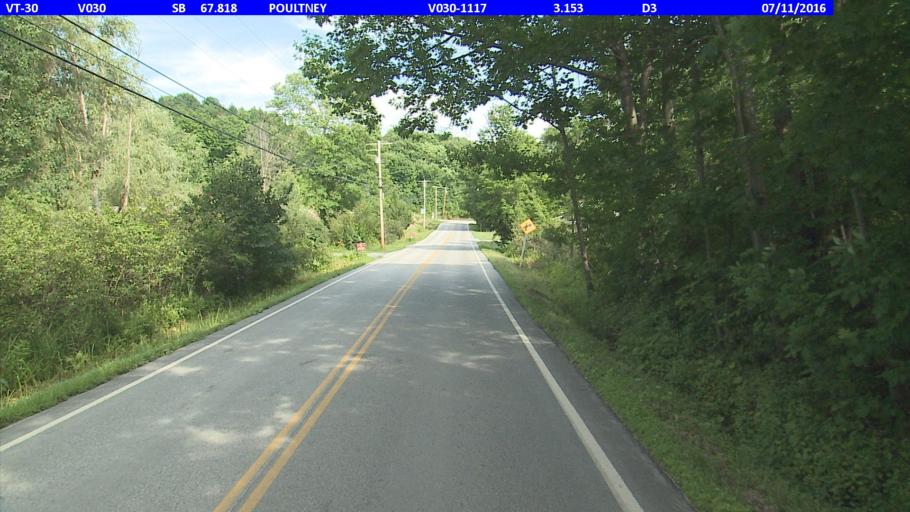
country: US
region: Vermont
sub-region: Rutland County
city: Poultney
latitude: 43.5061
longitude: -73.2123
